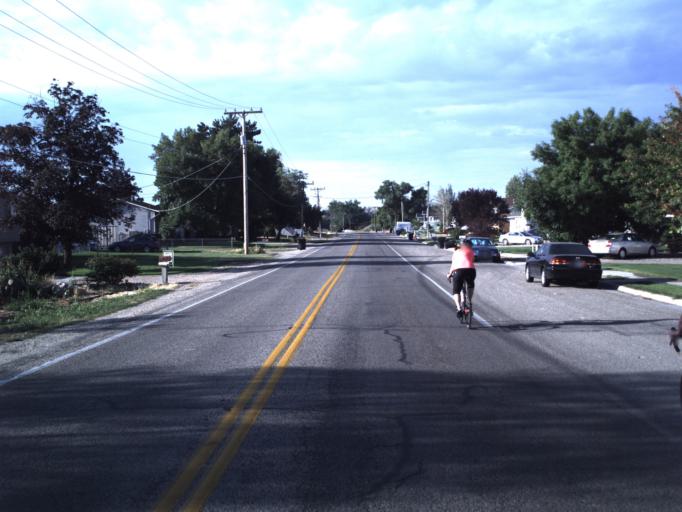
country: US
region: Utah
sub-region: Weber County
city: Plain City
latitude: 41.2851
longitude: -112.0933
